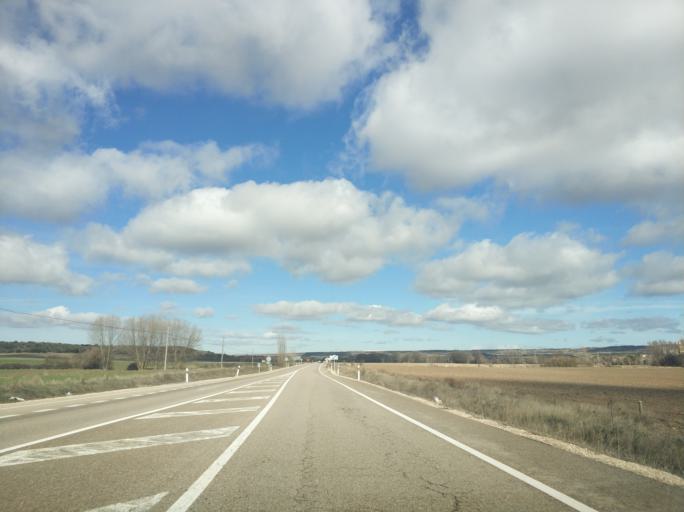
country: ES
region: Castille and Leon
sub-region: Provincia de Burgos
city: Revillarruz
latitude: 42.2378
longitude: -3.6699
